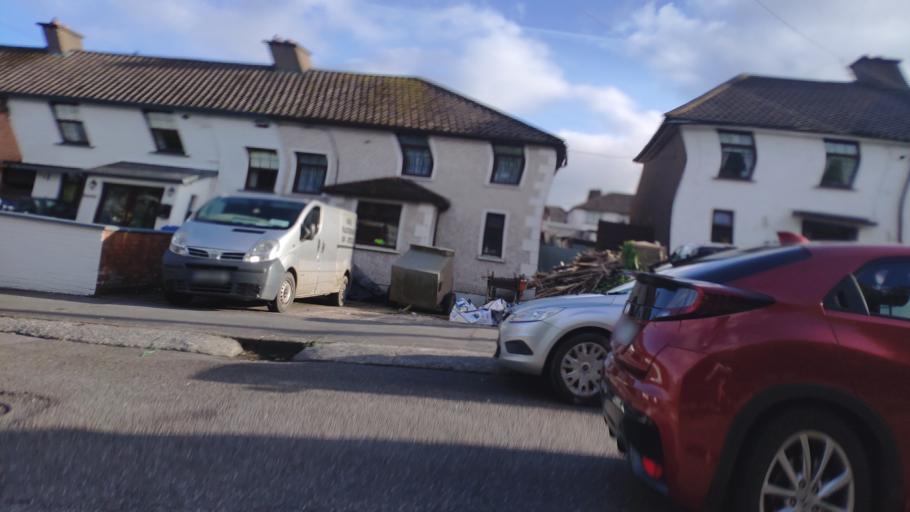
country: IE
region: Munster
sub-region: County Cork
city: Cork
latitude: 51.9063
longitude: -8.4949
